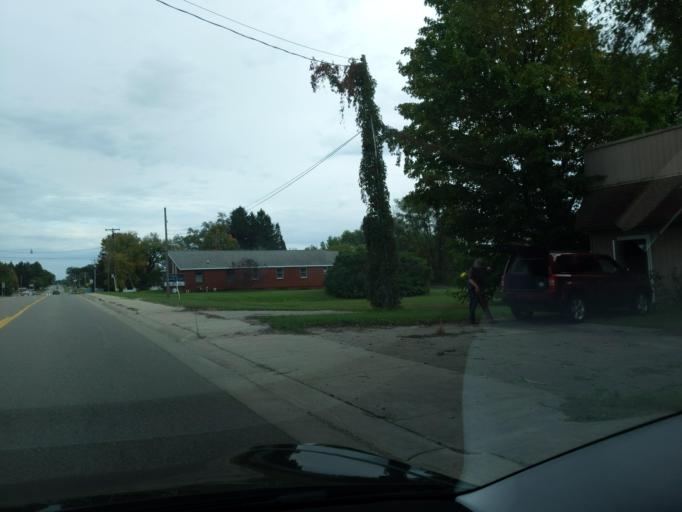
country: US
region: Michigan
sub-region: Clare County
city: Clare
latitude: 43.8345
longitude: -84.8620
